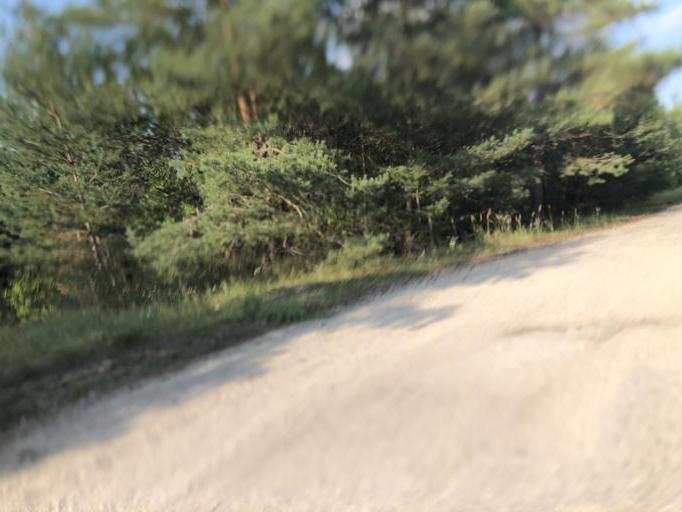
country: DE
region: Bavaria
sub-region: Regierungsbezirk Mittelfranken
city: Buckenhof
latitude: 49.5549
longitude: 11.0377
